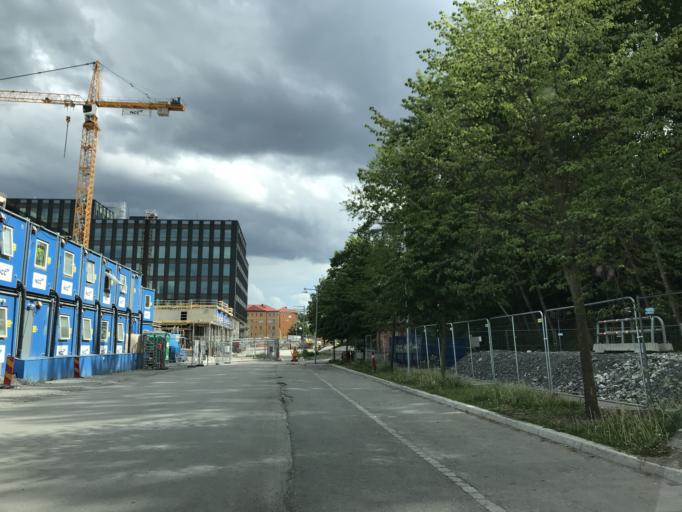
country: SE
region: Stockholm
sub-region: Solna Kommun
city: Solna
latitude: 59.3789
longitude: 18.0070
